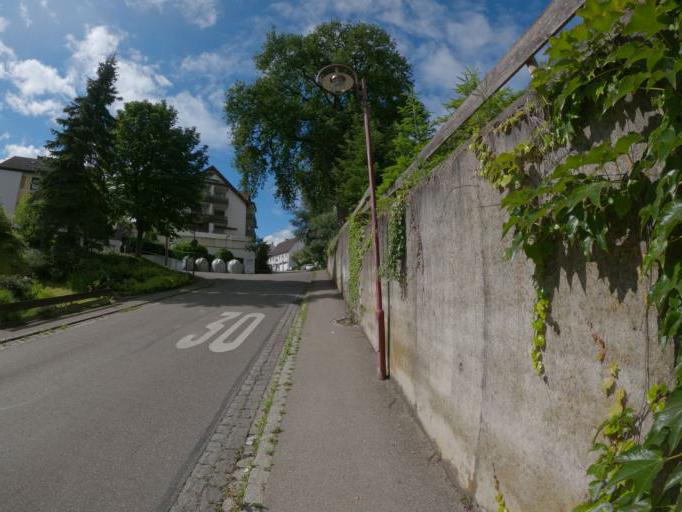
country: DE
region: Baden-Wuerttemberg
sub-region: Regierungsbezirk Stuttgart
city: Ebersbach an der Fils
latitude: 48.7074
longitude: 9.5244
